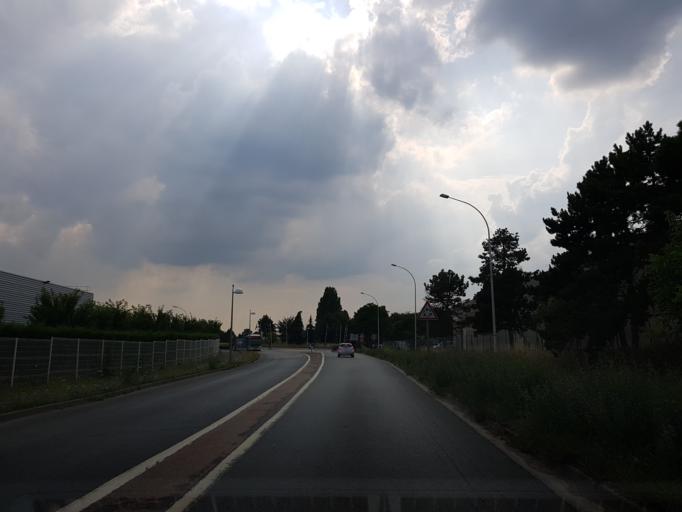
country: FR
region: Ile-de-France
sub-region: Departement de l'Essonne
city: Wissous
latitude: 48.7262
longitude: 2.3184
